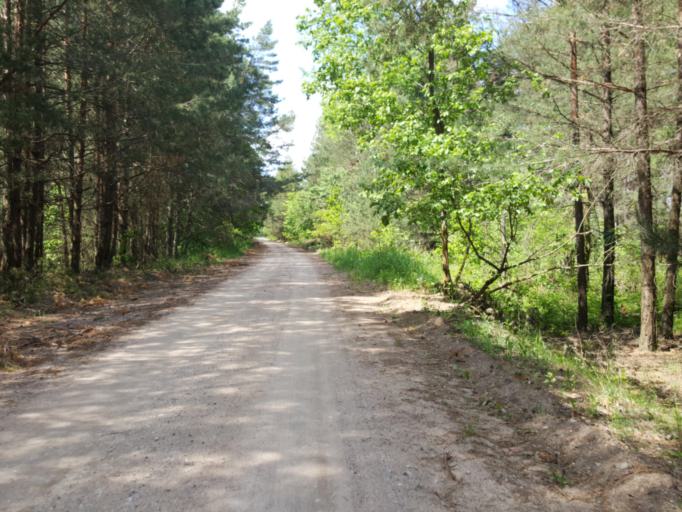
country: BY
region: Brest
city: Kamyanyuki
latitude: 52.5551
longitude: 23.6471
